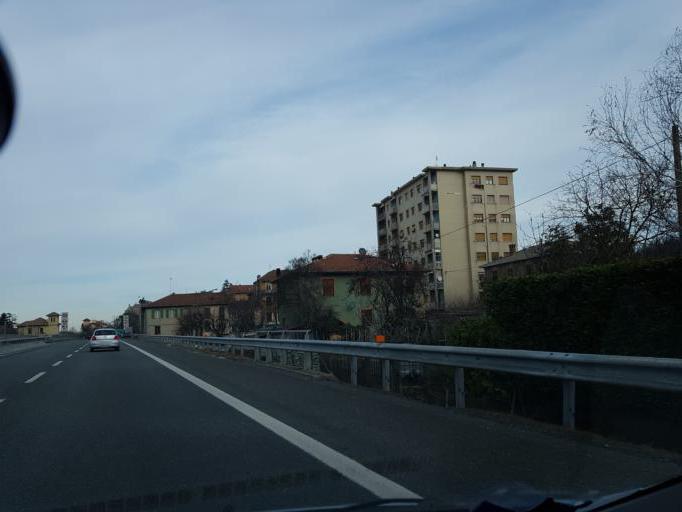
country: IT
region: Piedmont
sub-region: Provincia di Alessandria
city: Serravalle Scrivia
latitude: 44.7194
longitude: 8.8637
